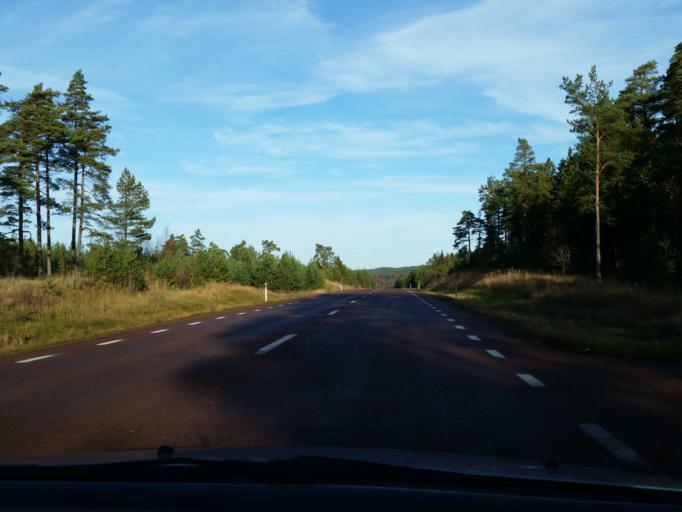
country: AX
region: Alands landsbygd
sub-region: Finstroem
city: Finstroem
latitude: 60.2862
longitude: 19.9528
